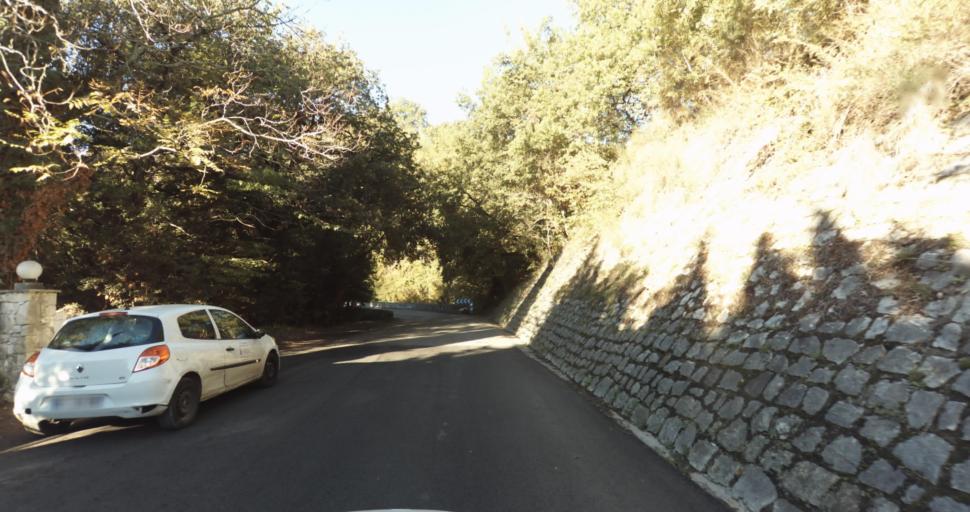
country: FR
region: Provence-Alpes-Cote d'Azur
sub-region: Departement des Alpes-Maritimes
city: Vence
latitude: 43.7277
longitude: 7.0878
